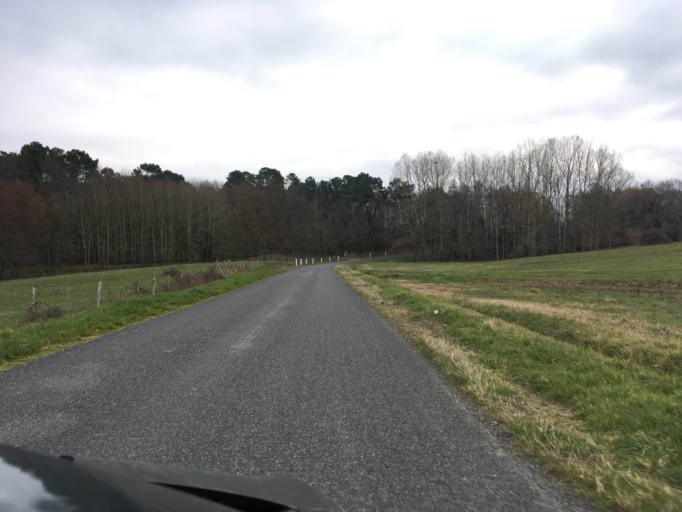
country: FR
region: Poitou-Charentes
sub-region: Departement de la Charente-Maritime
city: Mirambeau
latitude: 45.3298
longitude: -0.5845
